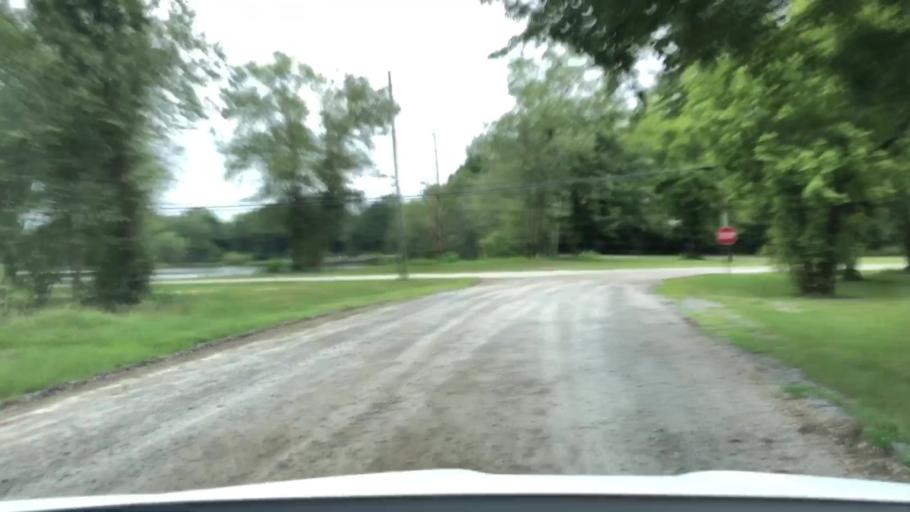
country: US
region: North Carolina
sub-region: Lenoir County
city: Kinston
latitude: 35.2598
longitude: -77.5935
